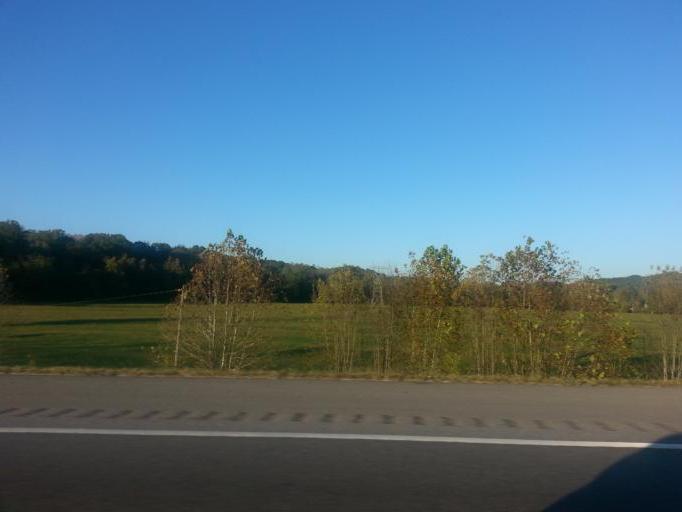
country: US
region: Tennessee
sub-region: Anderson County
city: Norris
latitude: 36.1405
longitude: -84.0458
